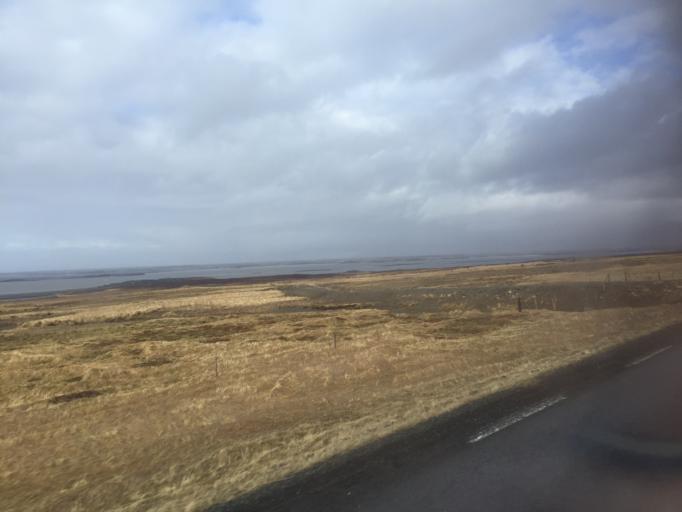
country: IS
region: West
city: Borgarnes
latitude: 64.4876
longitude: -21.9494
